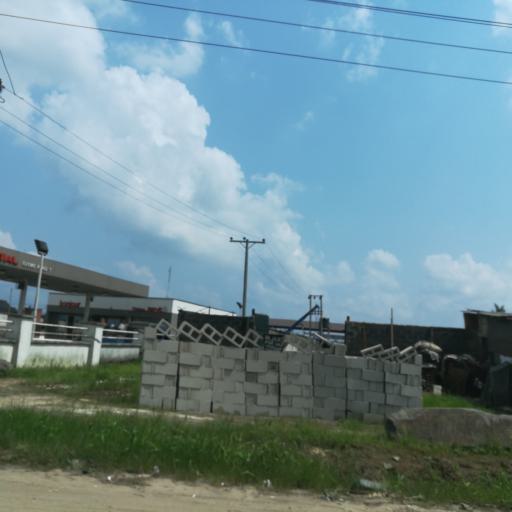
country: NG
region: Rivers
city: Port Harcourt
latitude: 4.8388
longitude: 7.0832
